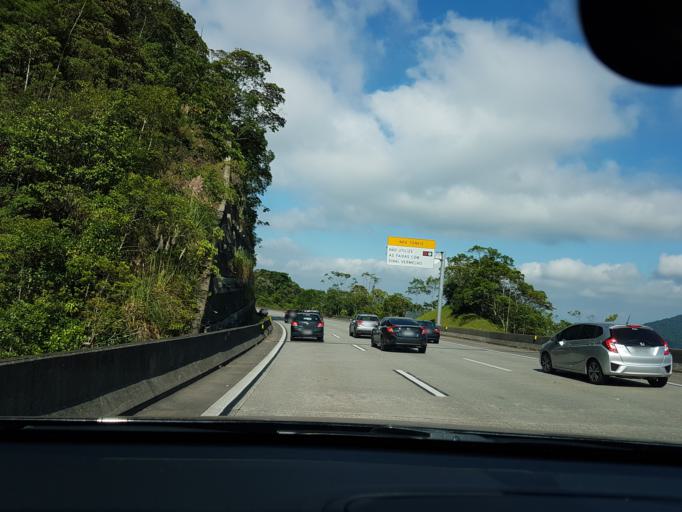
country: BR
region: Sao Paulo
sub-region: Cubatao
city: Cubatao
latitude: -23.9250
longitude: -46.5361
